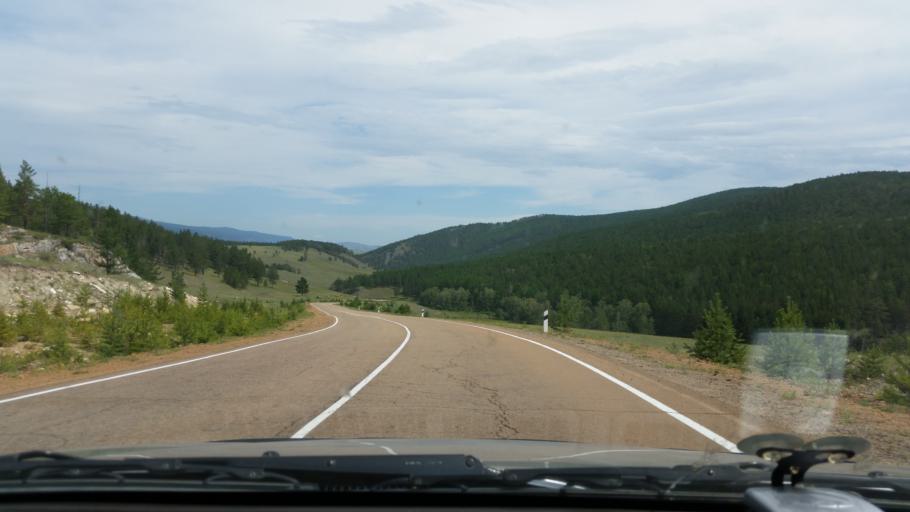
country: RU
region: Irkutsk
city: Yelantsy
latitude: 52.7660
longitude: 106.3533
